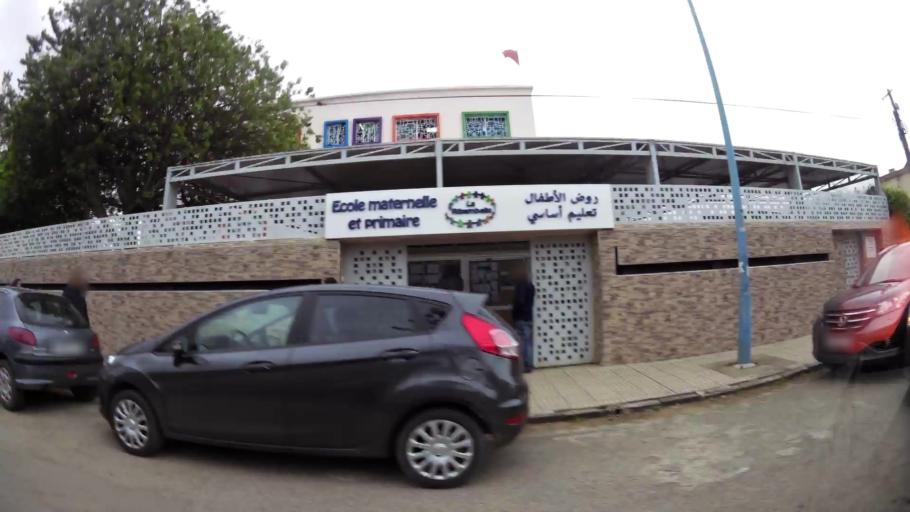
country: MA
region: Grand Casablanca
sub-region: Casablanca
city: Casablanca
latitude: 33.5682
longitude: -7.6209
